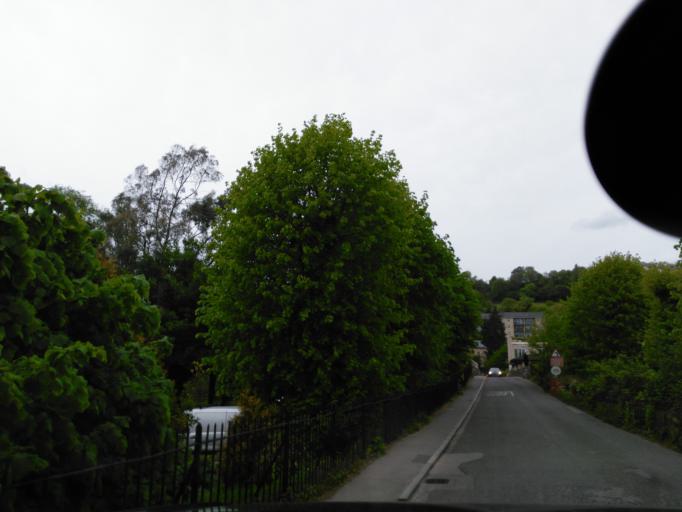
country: GB
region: England
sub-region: Bath and North East Somerset
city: Bath
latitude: 51.4008
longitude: -2.3248
